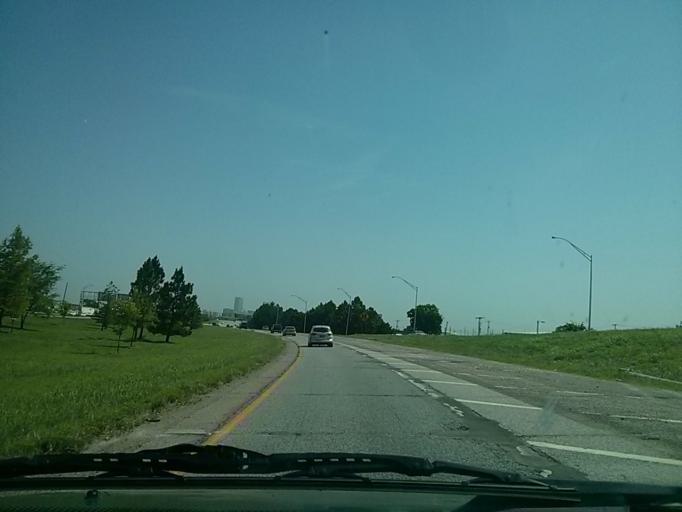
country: US
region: Oklahoma
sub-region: Tulsa County
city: Tulsa
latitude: 36.1123
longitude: -96.0119
